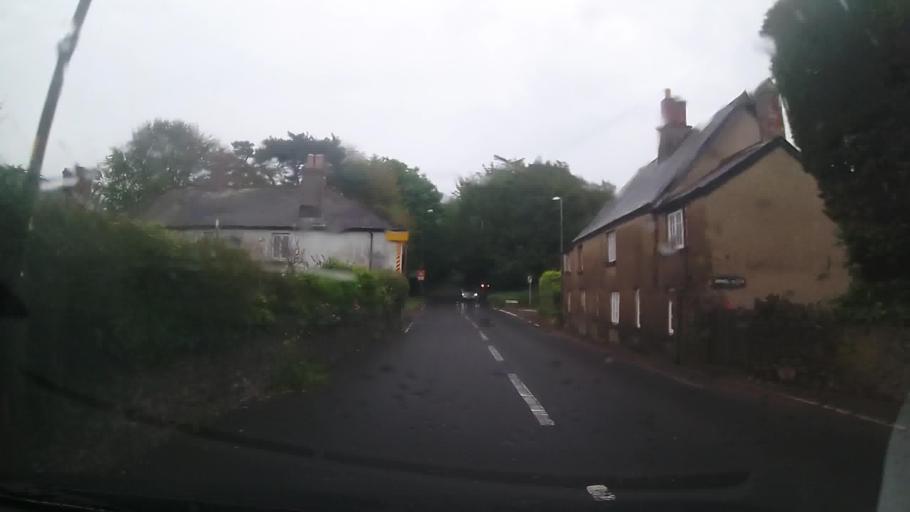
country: GB
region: England
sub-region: Borough of Torbay
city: Brixham
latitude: 50.3917
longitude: -3.5477
